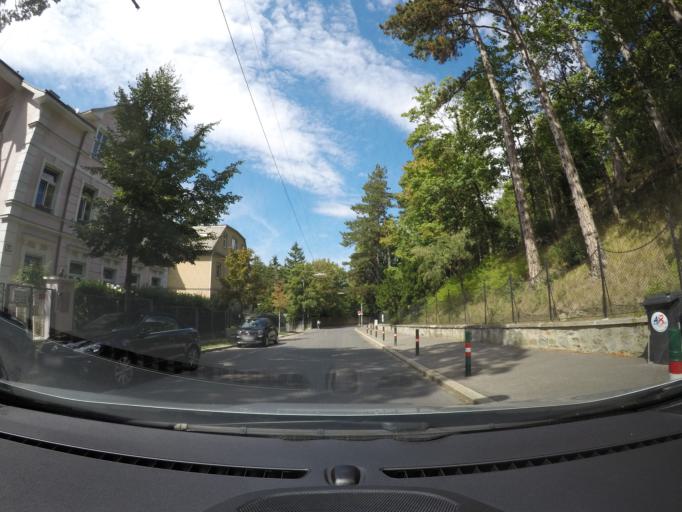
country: AT
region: Lower Austria
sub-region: Politischer Bezirk Modling
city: Perchtoldsdorf
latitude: 48.1847
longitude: 16.2650
